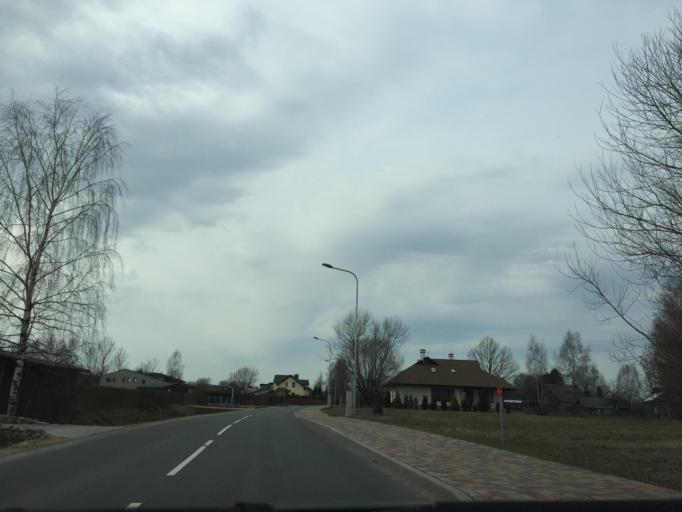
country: LV
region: Kekava
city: Balozi
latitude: 56.8829
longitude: 24.1699
